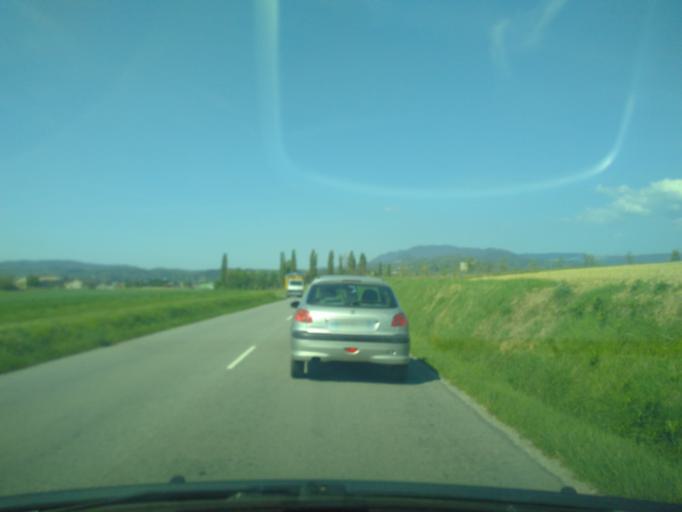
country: FR
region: Rhone-Alpes
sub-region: Departement de la Drome
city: Crest
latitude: 44.7085
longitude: 5.0067
